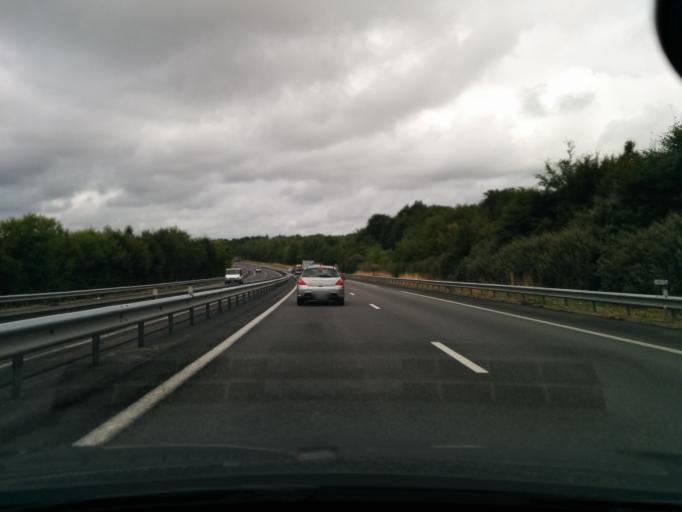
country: FR
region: Limousin
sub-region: Departement de la Haute-Vienne
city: Saint-Germain-les-Belles
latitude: 45.5189
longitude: 1.5169
